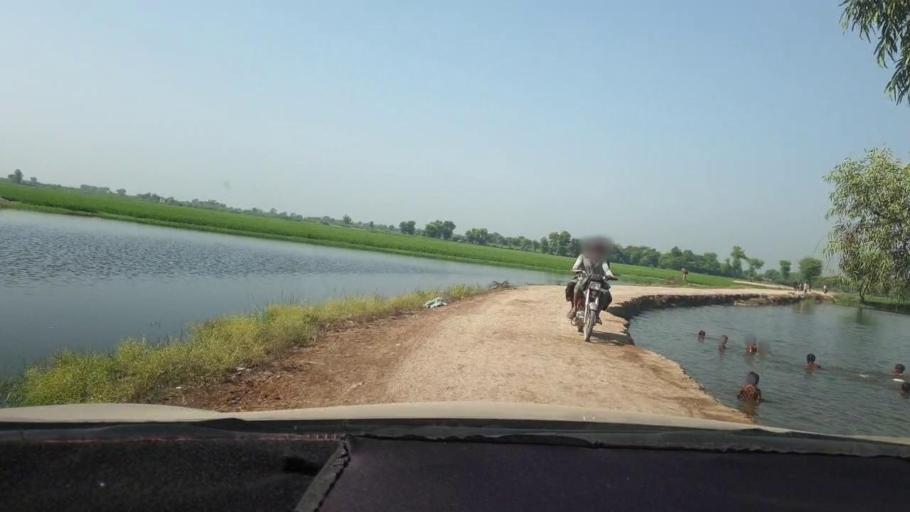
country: PK
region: Sindh
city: Miro Khan
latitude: 27.7050
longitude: 68.0933
